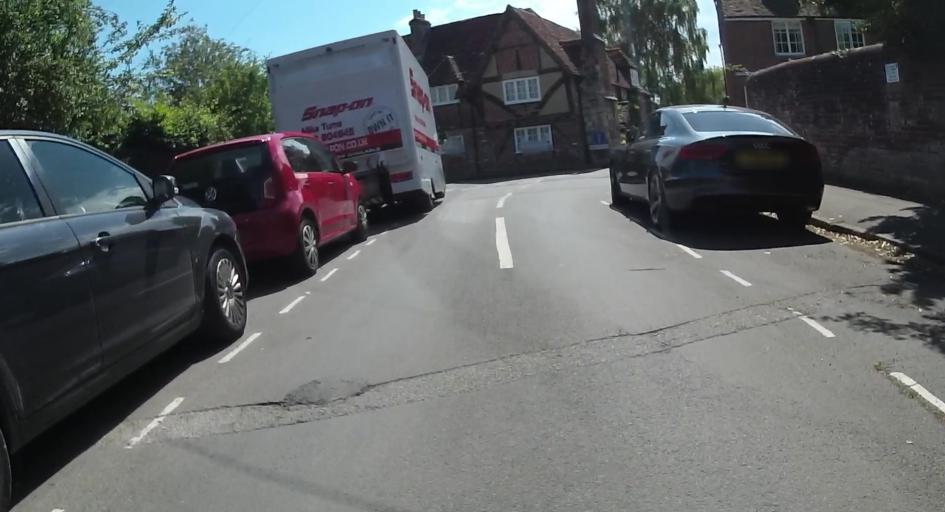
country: GB
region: England
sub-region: Hampshire
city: Winchester
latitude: 51.0501
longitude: -1.3210
